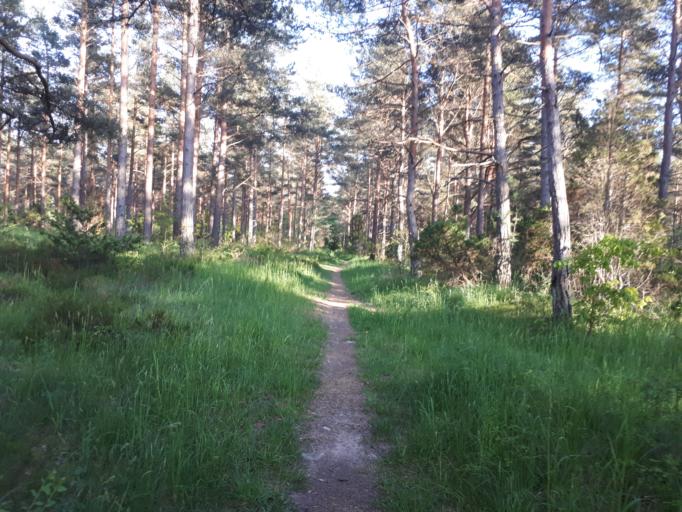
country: SE
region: Gotland
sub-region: Gotland
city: Visby
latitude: 57.6043
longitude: 18.2984
